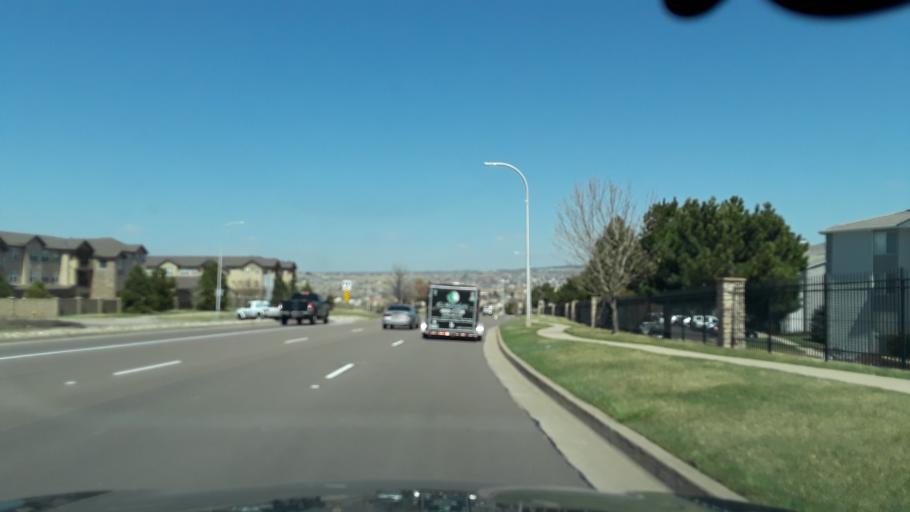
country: US
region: Colorado
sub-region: El Paso County
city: Cimarron Hills
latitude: 38.9213
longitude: -104.7384
